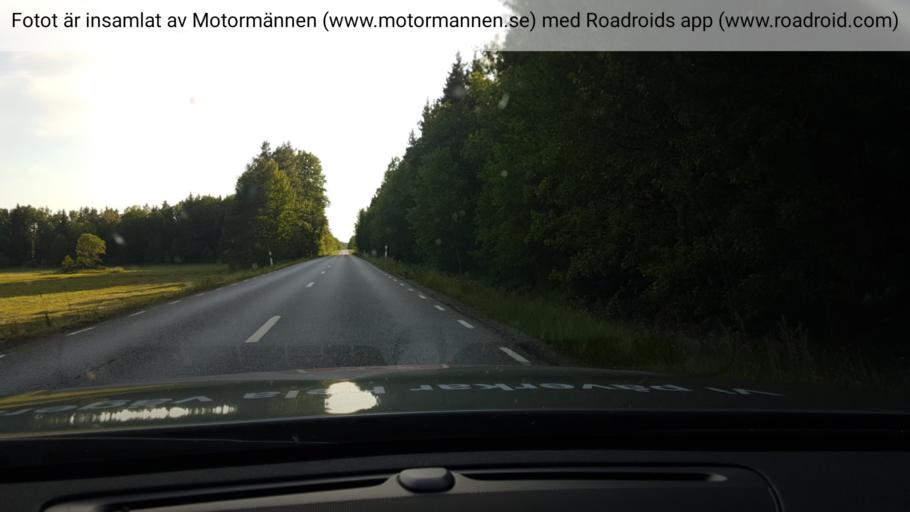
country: SE
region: Uppsala
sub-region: Osthammars Kommun
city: Gimo
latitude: 59.9501
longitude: 18.0333
